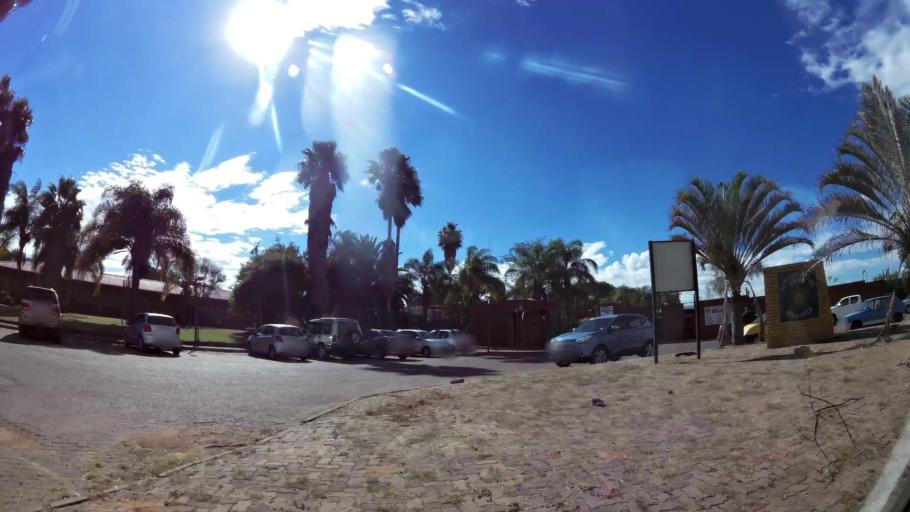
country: ZA
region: Limpopo
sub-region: Waterberg District Municipality
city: Bela-Bela
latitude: -24.8784
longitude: 28.2937
